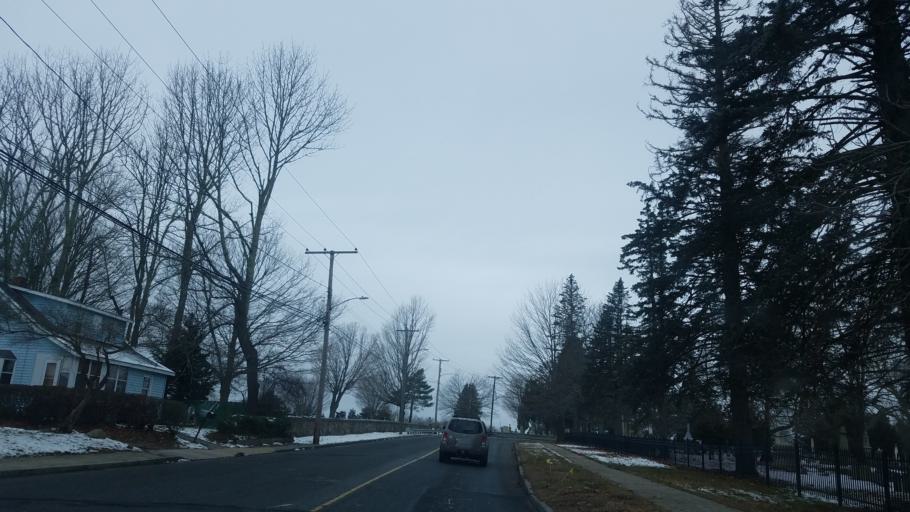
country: US
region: Connecticut
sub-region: New London County
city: Central Waterford
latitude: 41.3606
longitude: -72.1236
